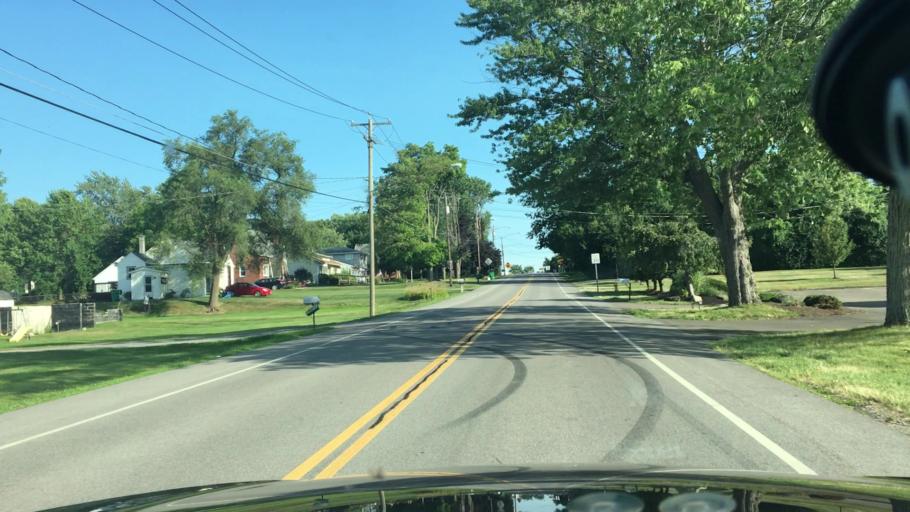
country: US
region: New York
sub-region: Erie County
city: Wanakah
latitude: 42.7696
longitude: -78.8671
